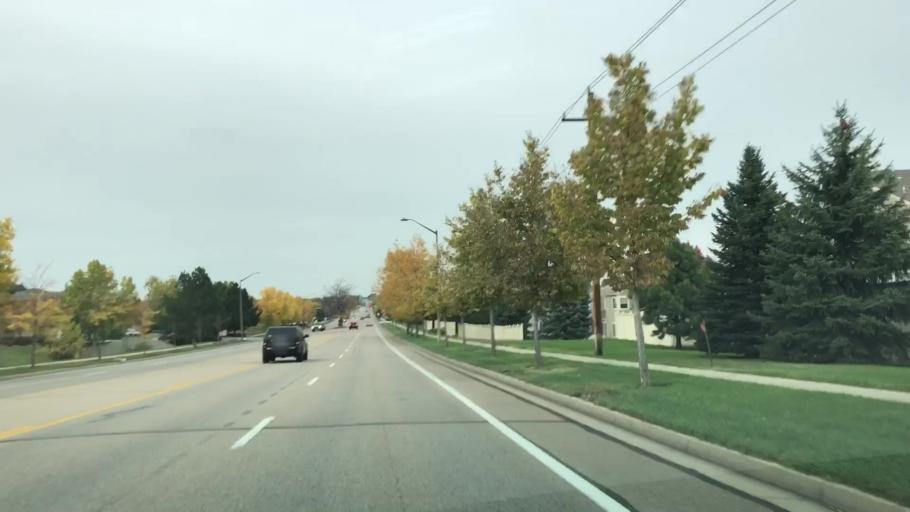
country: US
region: Colorado
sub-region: Larimer County
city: Loveland
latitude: 40.4917
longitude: -105.0582
